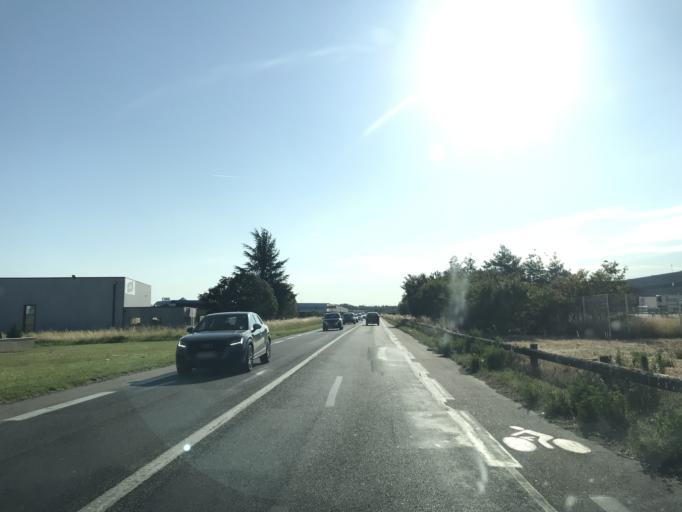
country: FR
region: Rhone-Alpes
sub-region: Departement du Rhone
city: Mions
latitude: 45.6514
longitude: 4.9289
